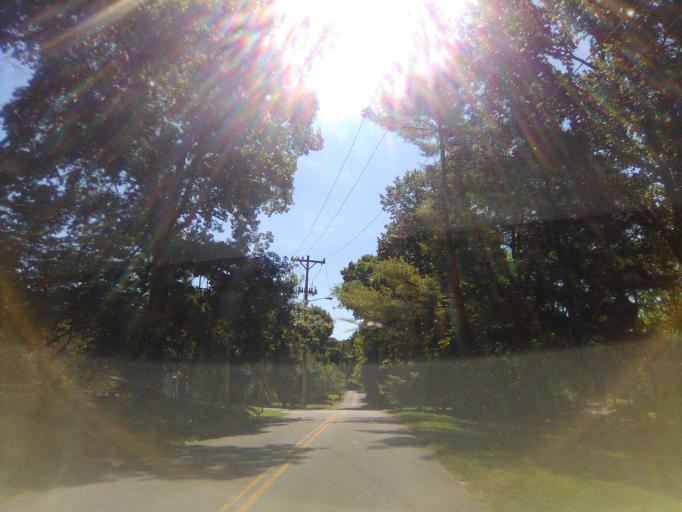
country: US
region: Tennessee
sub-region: Davidson County
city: Belle Meade
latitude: 36.1197
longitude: -86.8327
